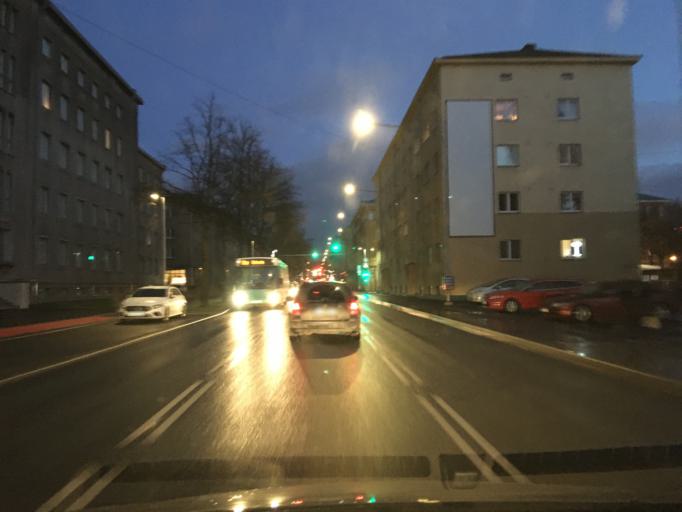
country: EE
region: Harju
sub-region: Tallinna linn
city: Tallinn
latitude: 59.4338
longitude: 24.7721
